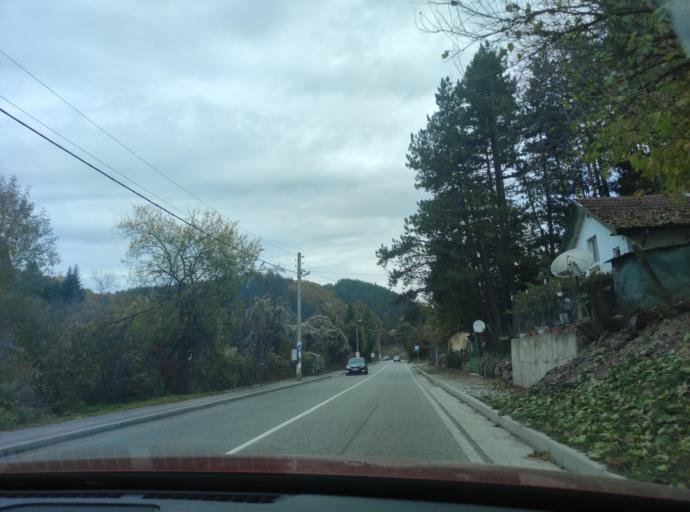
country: BG
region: Sofiya
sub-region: Obshtina Godech
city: Godech
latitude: 42.9727
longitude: 23.1405
